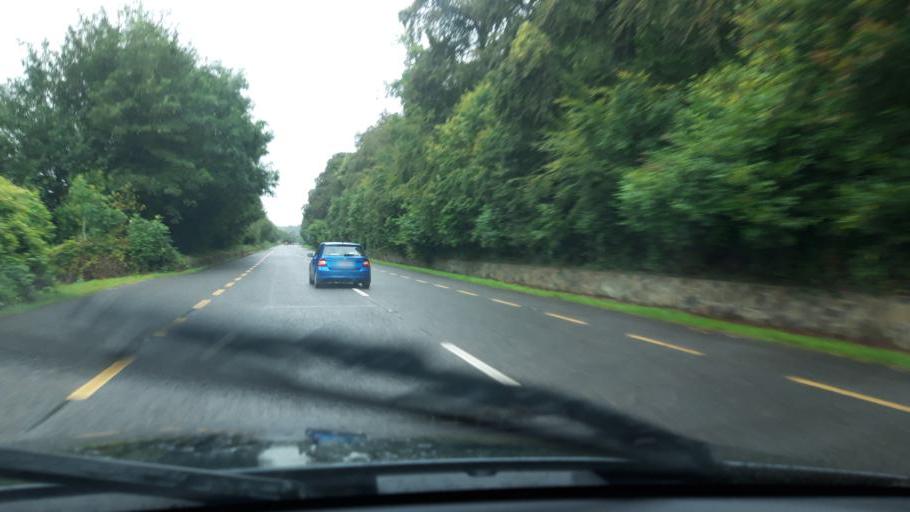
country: IE
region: Munster
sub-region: County Cork
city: Youghal
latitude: 52.1460
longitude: -7.8963
